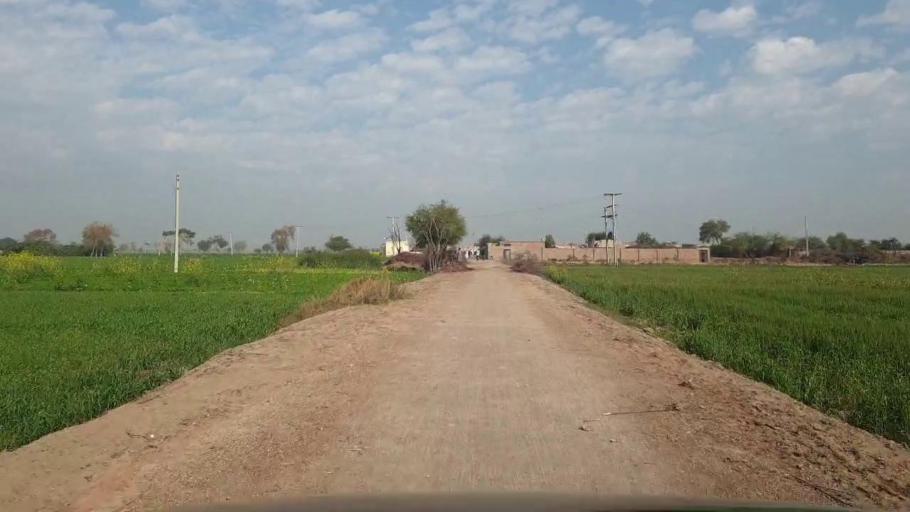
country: PK
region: Sindh
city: Hala
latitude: 25.9921
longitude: 68.3864
